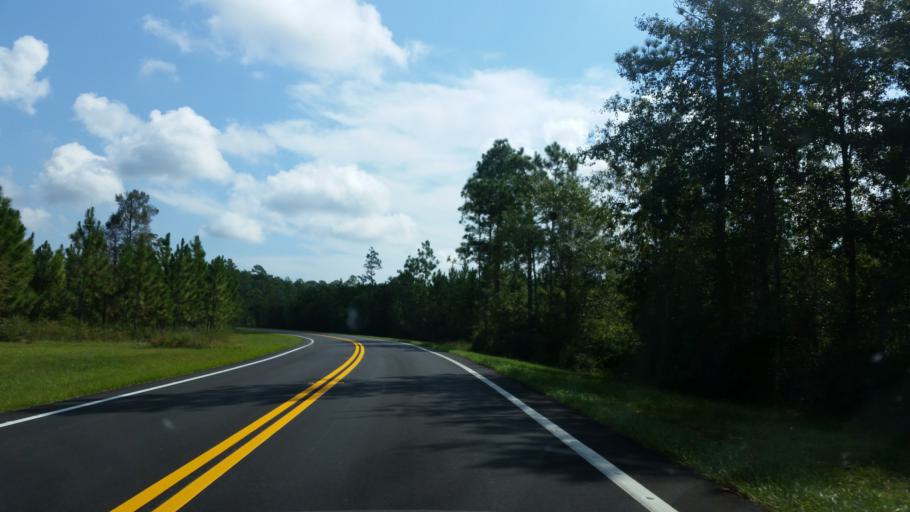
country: US
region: Florida
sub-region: Escambia County
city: Molino
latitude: 30.6943
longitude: -87.4324
